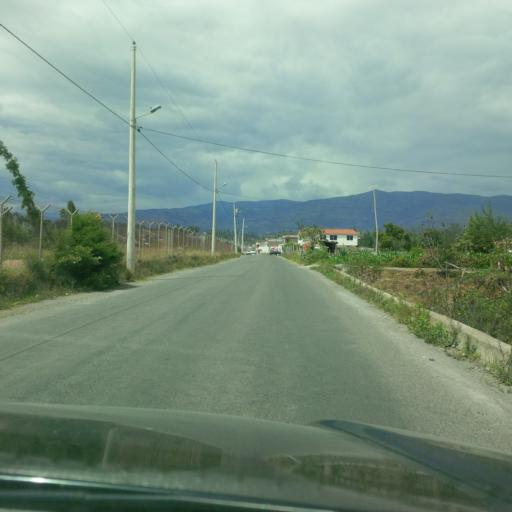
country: EC
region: Chimborazo
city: Riobamba
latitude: -1.6454
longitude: -78.6519
